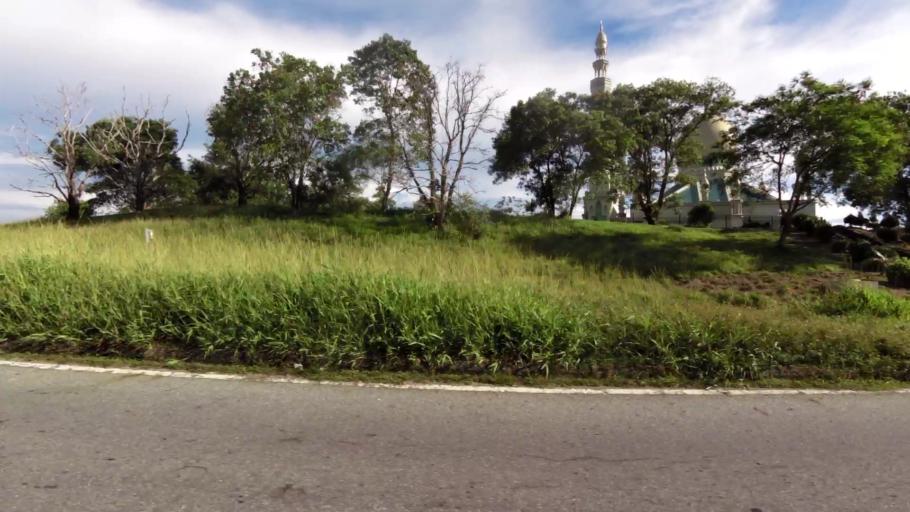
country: BN
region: Brunei and Muara
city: Bandar Seri Begawan
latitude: 4.9722
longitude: 114.9672
